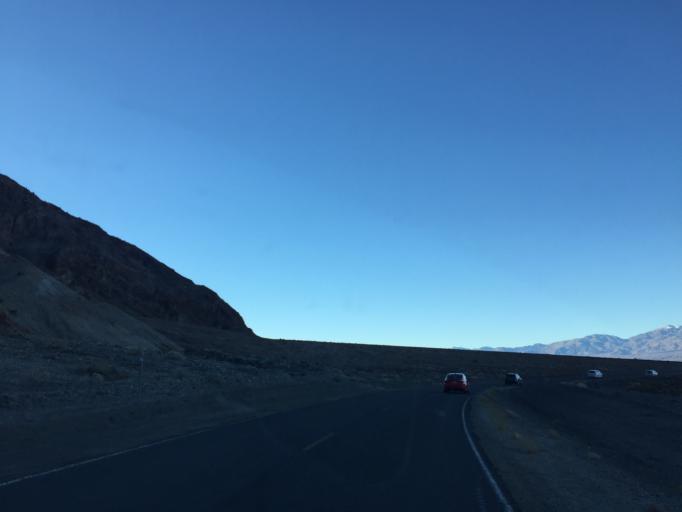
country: US
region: Nevada
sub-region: Nye County
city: Beatty
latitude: 36.1736
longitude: -116.7638
